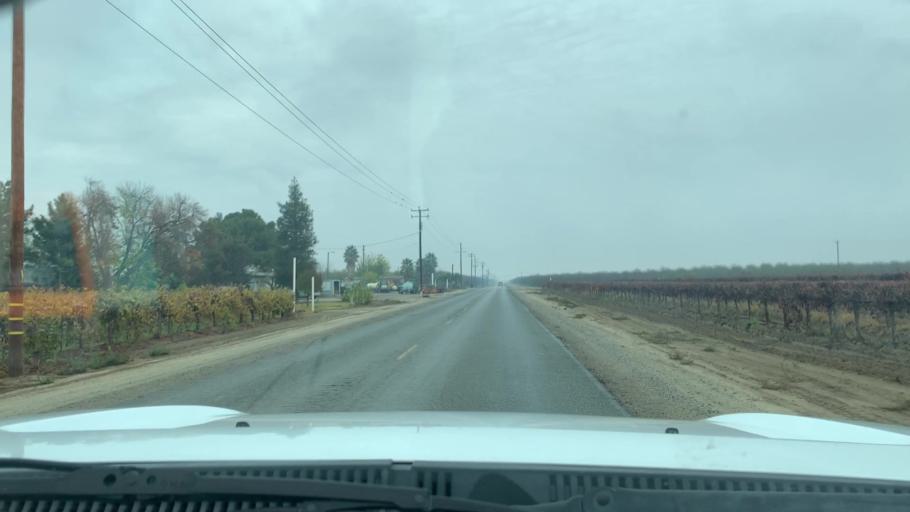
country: US
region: California
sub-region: Kern County
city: Delano
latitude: 35.7611
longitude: -119.3676
